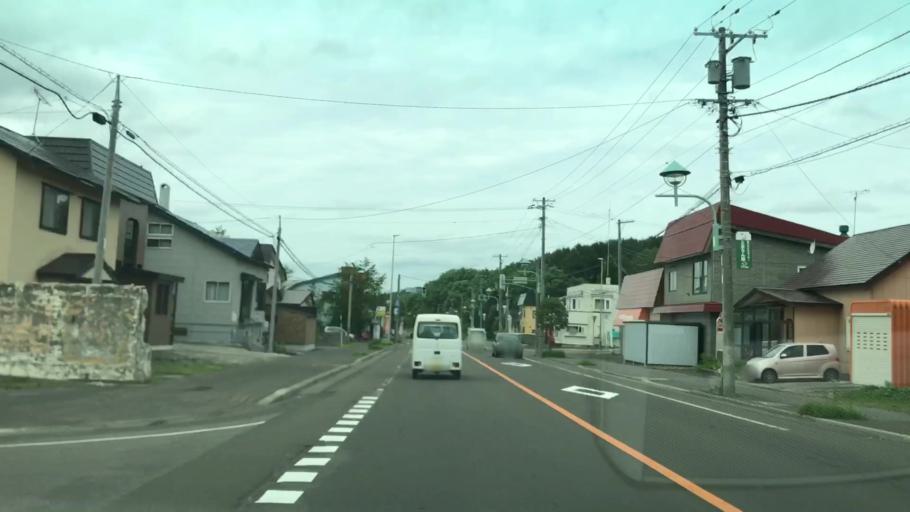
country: JP
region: Hokkaido
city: Iwanai
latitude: 42.9703
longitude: 140.6778
